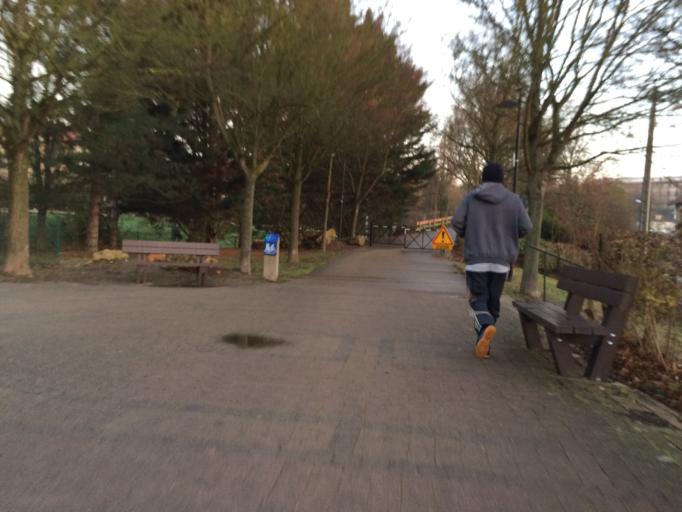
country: FR
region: Ile-de-France
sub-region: Departement des Hauts-de-Seine
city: Fontenay-aux-Roses
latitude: 48.7864
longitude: 2.2899
